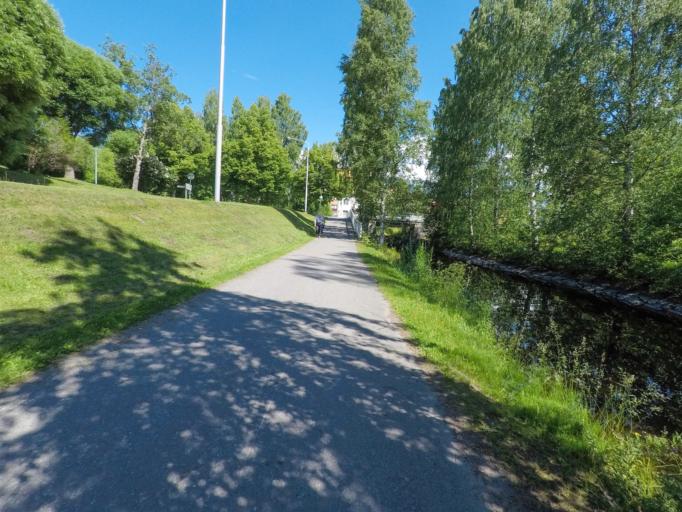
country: FI
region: Southern Savonia
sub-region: Savonlinna
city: Savonlinna
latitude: 61.8698
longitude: 28.8971
